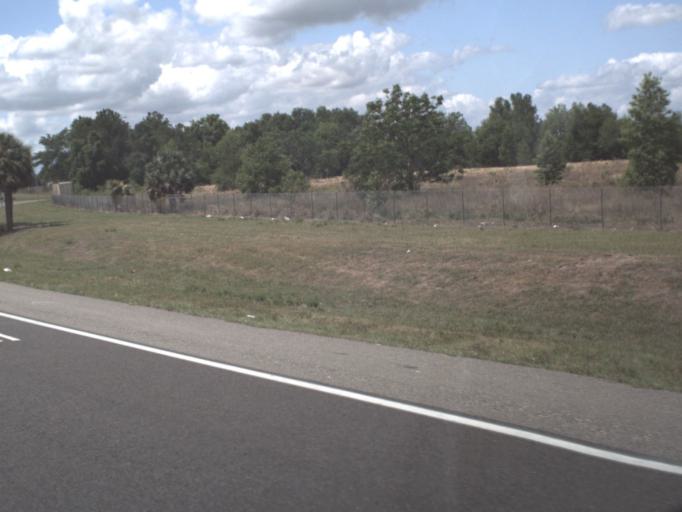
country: US
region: Florida
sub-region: Orange County
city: Paradise Heights
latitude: 28.6049
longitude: -81.5383
